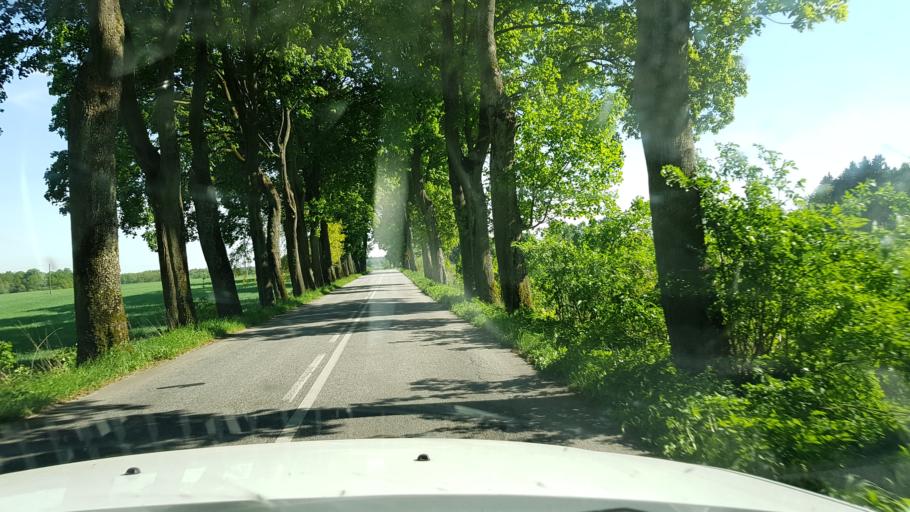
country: PL
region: West Pomeranian Voivodeship
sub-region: Powiat lobeski
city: Resko
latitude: 53.8324
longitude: 15.3874
